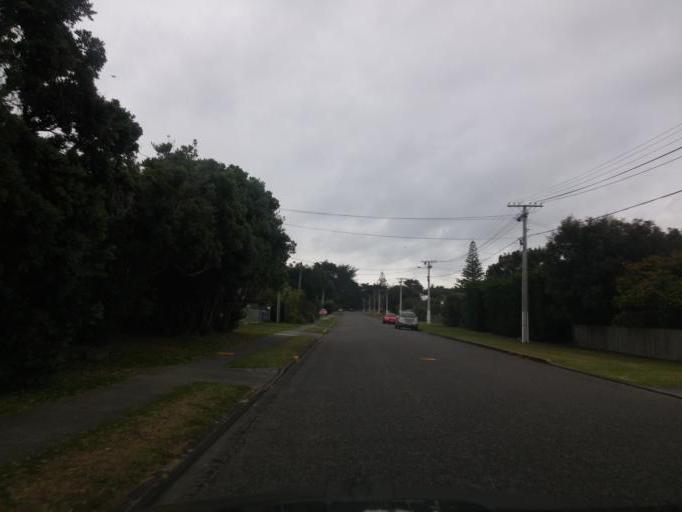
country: NZ
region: Wellington
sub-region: Kapiti Coast District
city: Paraparaumu
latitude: -40.8650
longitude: 175.0258
